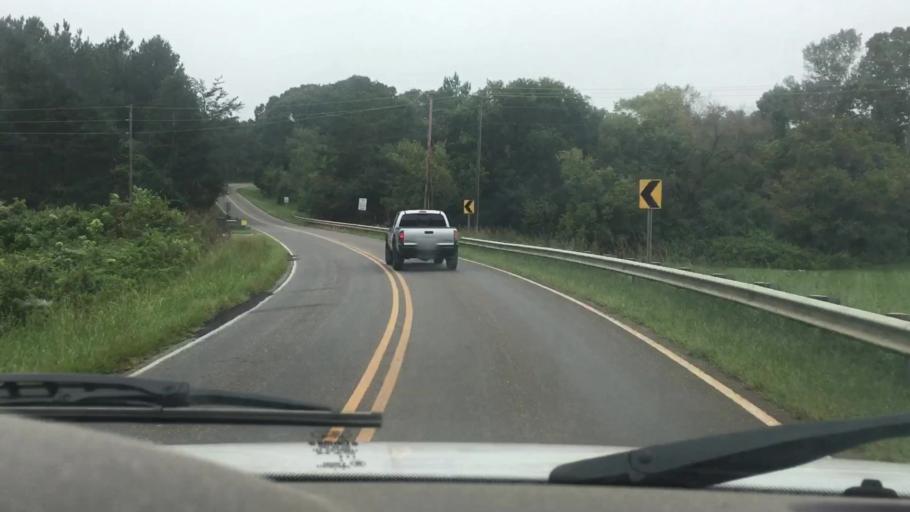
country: US
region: North Carolina
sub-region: Gaston County
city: Davidson
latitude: 35.5245
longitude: -80.7801
